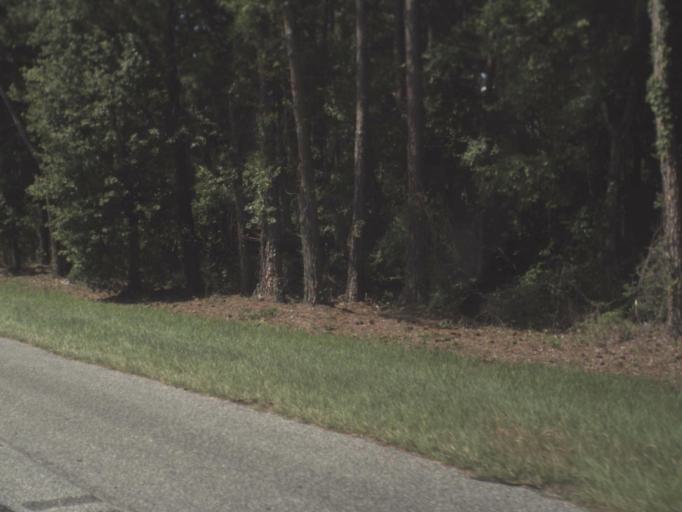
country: US
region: Florida
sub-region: Saint Johns County
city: Villano Beach
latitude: 29.9953
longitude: -81.4676
